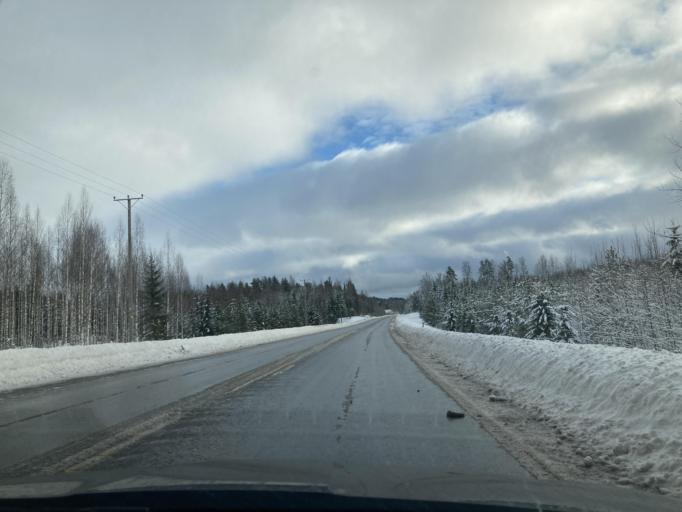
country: FI
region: Central Finland
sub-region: Jaemsae
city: Jaemsae
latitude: 61.7669
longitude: 25.2389
